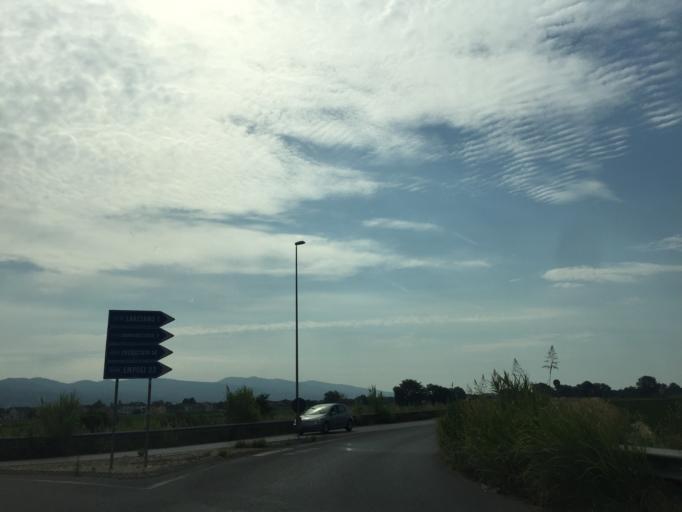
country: IT
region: Tuscany
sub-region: Provincia di Pistoia
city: Uggia-Pazzera-Bizzarrino
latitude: 43.8310
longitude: 10.8282
